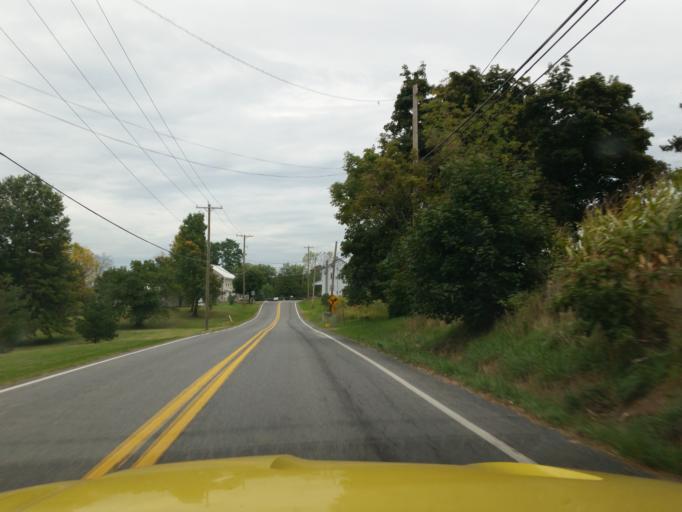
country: US
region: Pennsylvania
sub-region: Lebanon County
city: Fredericksburg
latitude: 40.4500
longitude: -76.3449
